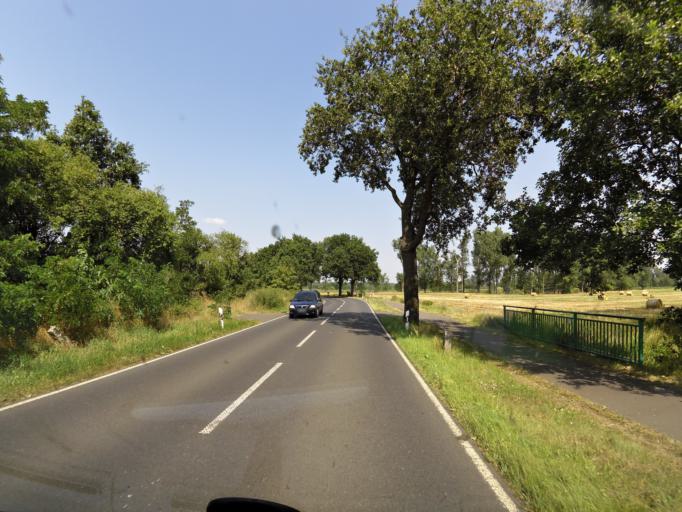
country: DE
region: Brandenburg
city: Liebenwalde
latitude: 52.8536
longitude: 13.3311
